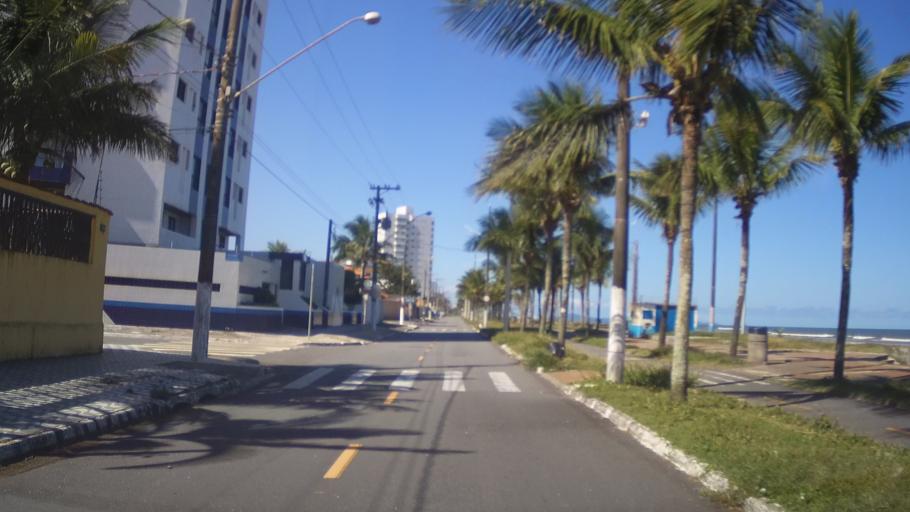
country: BR
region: Sao Paulo
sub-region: Mongagua
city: Mongagua
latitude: -24.0861
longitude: -46.5998
